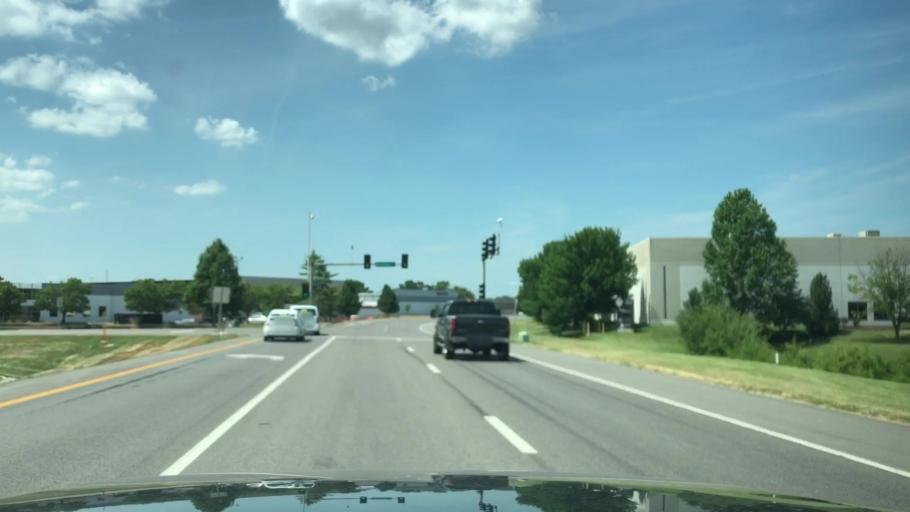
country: US
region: Missouri
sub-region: Saint Charles County
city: Saint Charles
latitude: 38.7722
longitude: -90.4590
